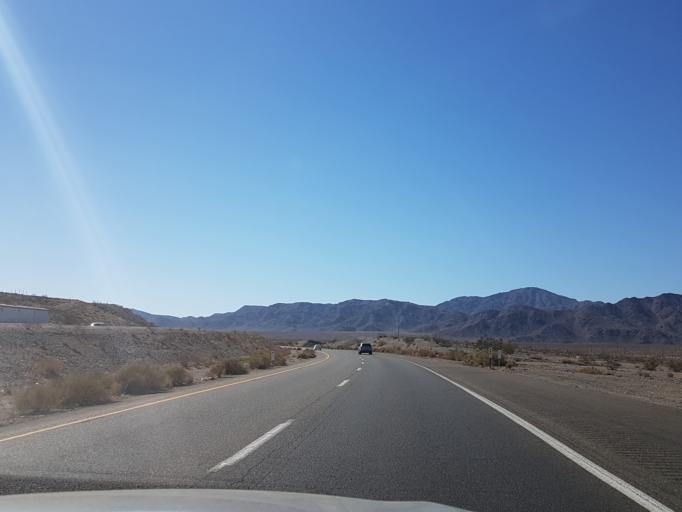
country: US
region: California
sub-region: San Bernardino County
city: Fort Irwin
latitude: 35.1949
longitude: -116.1501
